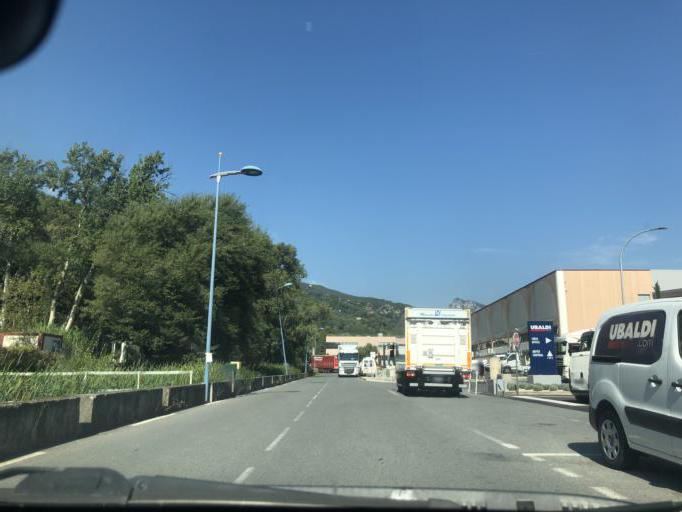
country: FR
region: Provence-Alpes-Cote d'Azur
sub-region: Departement des Alpes-Maritimes
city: Saint-Martin-du-Var
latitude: 43.8068
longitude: 7.1857
